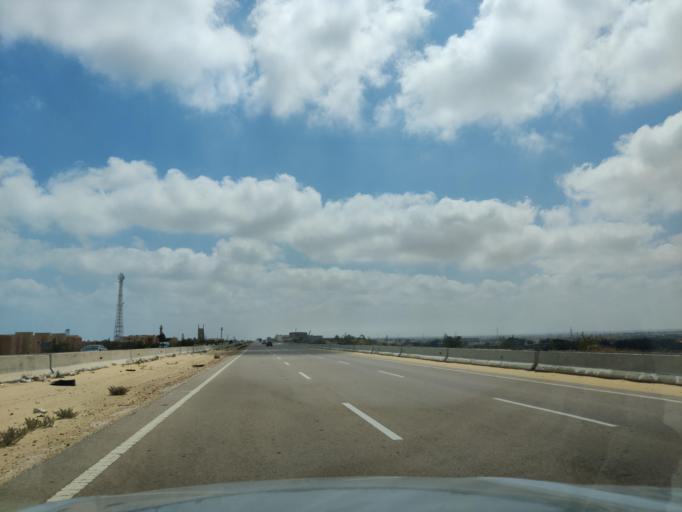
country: EG
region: Muhafazat Matruh
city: Al `Alamayn
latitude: 30.8169
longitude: 29.1439
